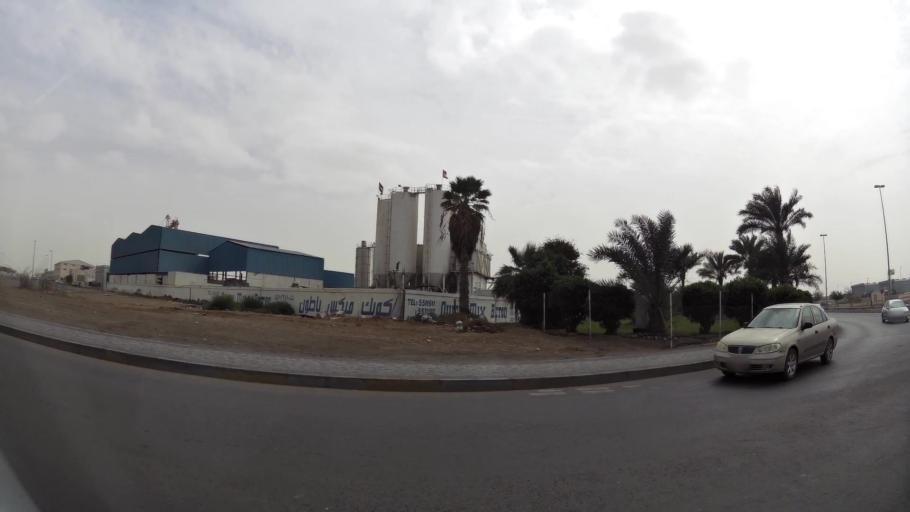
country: AE
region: Abu Dhabi
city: Abu Dhabi
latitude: 24.3581
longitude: 54.4825
